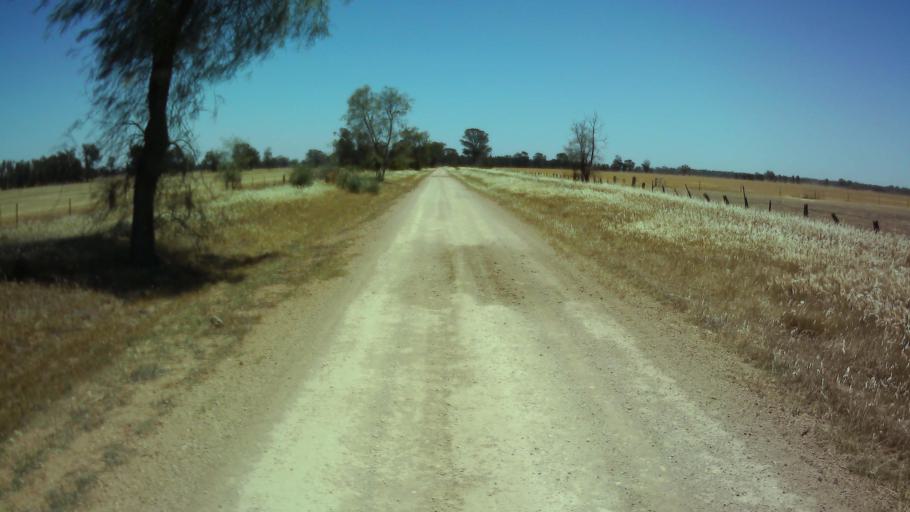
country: AU
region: New South Wales
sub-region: Weddin
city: Grenfell
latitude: -33.9918
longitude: 147.9526
